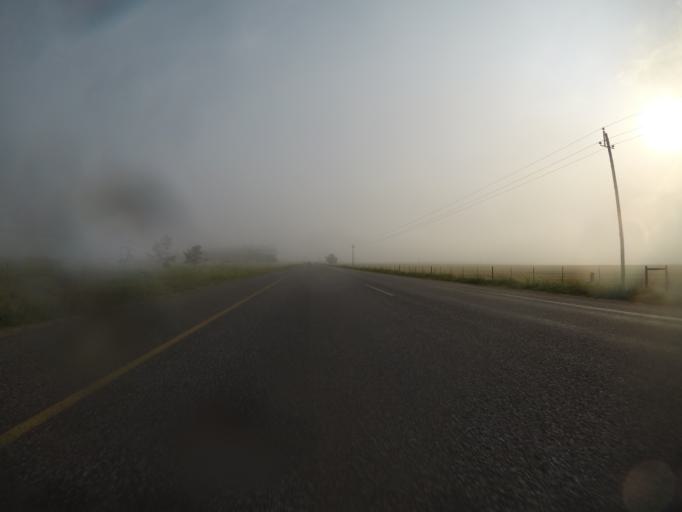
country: ZA
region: Western Cape
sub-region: City of Cape Town
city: Kraaifontein
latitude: -33.6692
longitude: 18.7073
